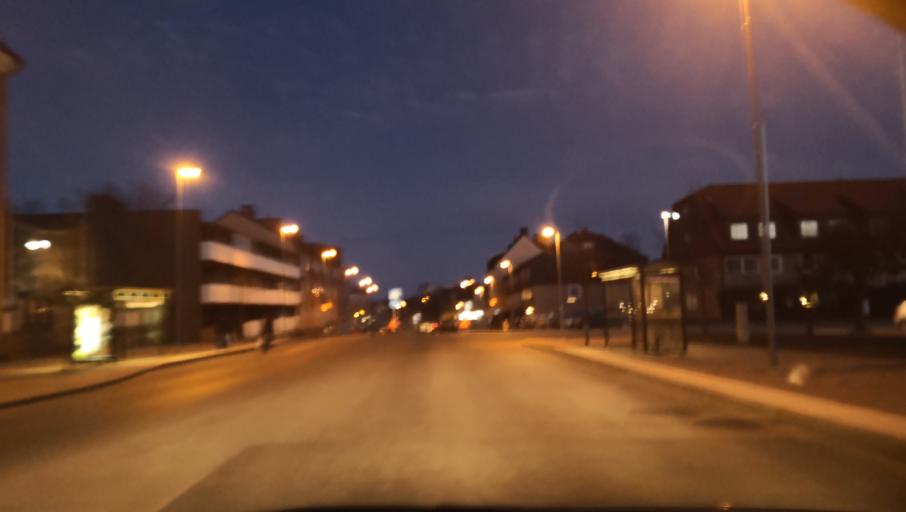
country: SE
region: Stockholm
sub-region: Nynashamns Kommun
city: Nynashamn
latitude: 58.9124
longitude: 17.9492
